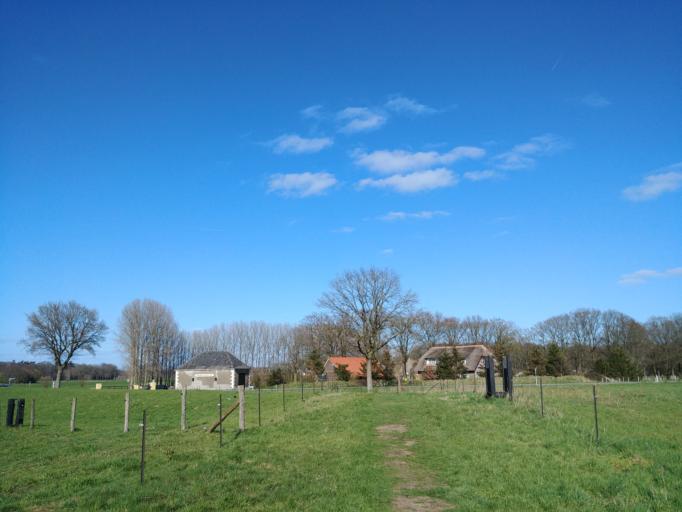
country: NL
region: Overijssel
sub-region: Gemeente Olst-Wijhe
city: Boskamp
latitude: 52.2886
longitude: 6.1206
